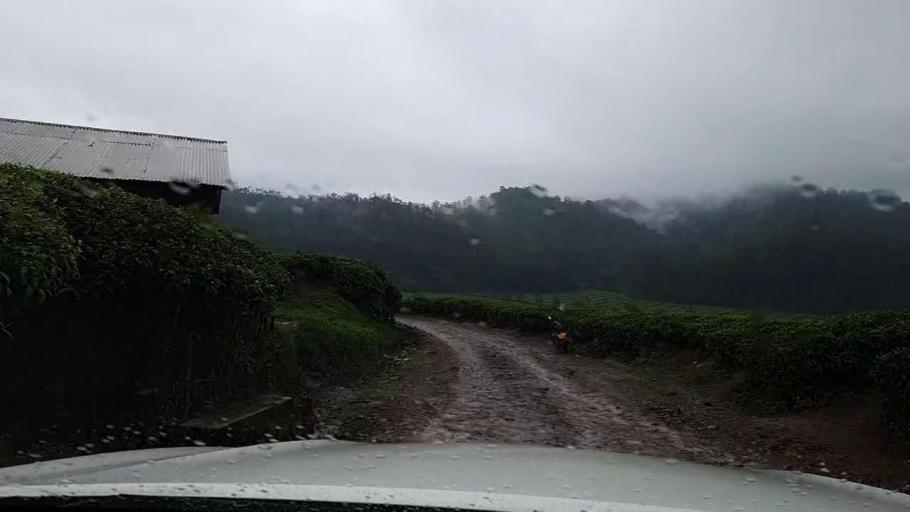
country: RW
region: Western Province
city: Cyangugu
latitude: -2.4577
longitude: 29.0388
